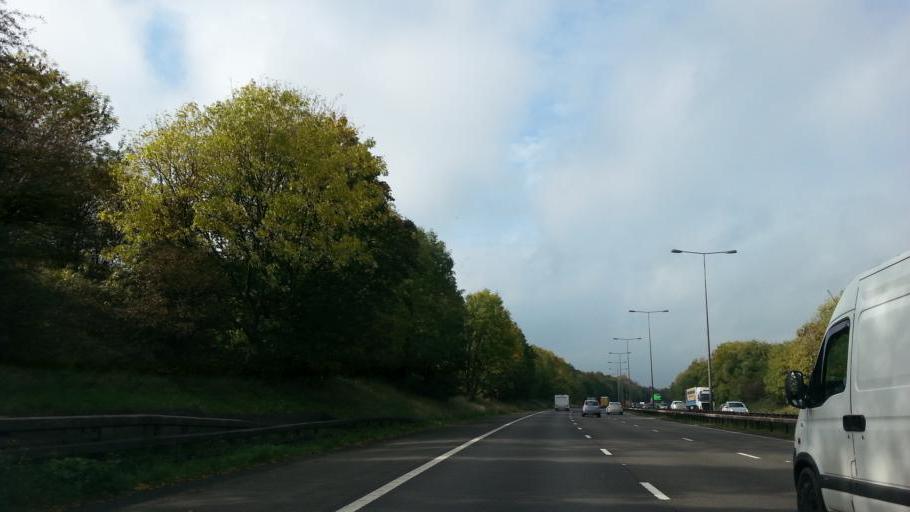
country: GB
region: England
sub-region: Staffordshire
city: Audley
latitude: 52.9937
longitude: -2.3003
